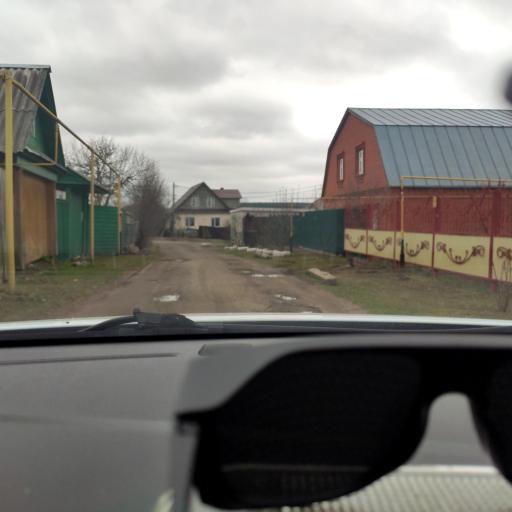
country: RU
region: Tatarstan
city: Vysokaya Gora
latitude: 55.8687
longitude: 49.2482
